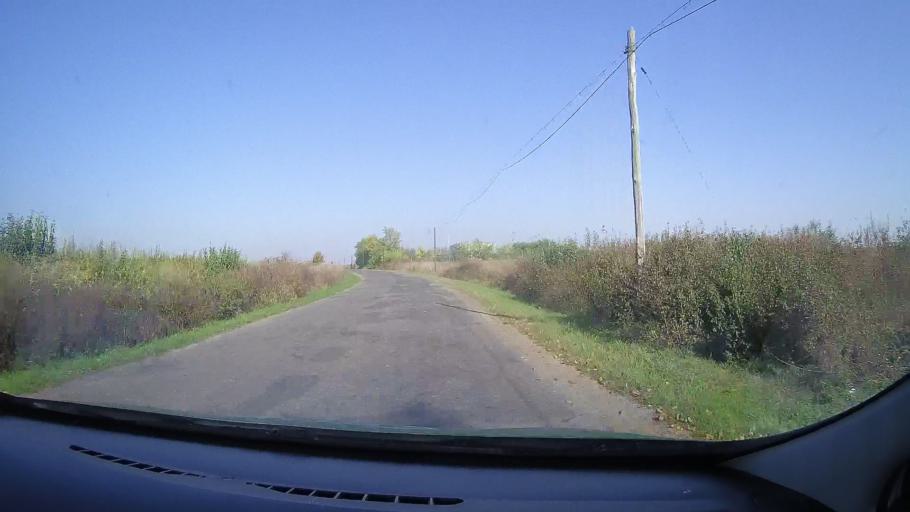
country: RO
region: Satu Mare
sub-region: Comuna Ciumesti
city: Ciumesti
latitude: 47.6487
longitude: 22.3371
